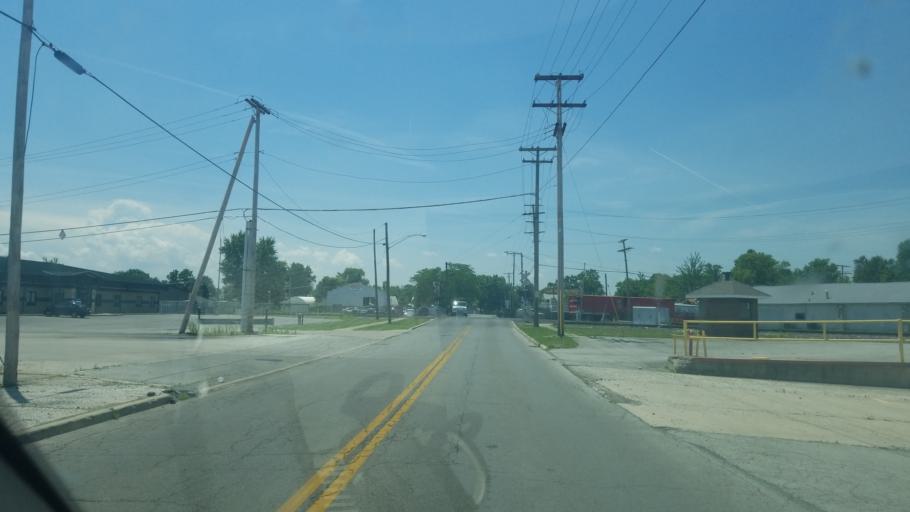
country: US
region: Ohio
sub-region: Hancock County
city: Findlay
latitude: 41.0493
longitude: -83.6449
